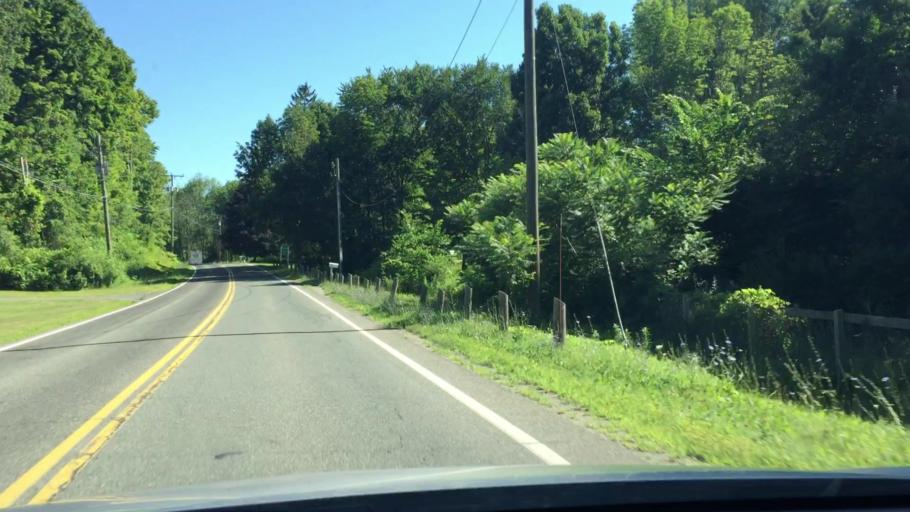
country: US
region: Massachusetts
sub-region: Berkshire County
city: Lenox
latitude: 42.4105
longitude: -73.3137
